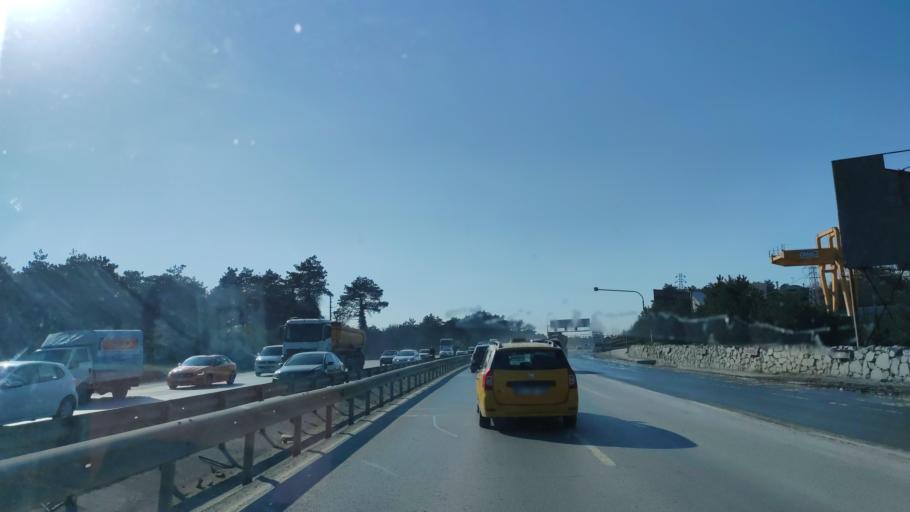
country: TR
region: Istanbul
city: Basaksehir
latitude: 41.1607
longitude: 28.7777
